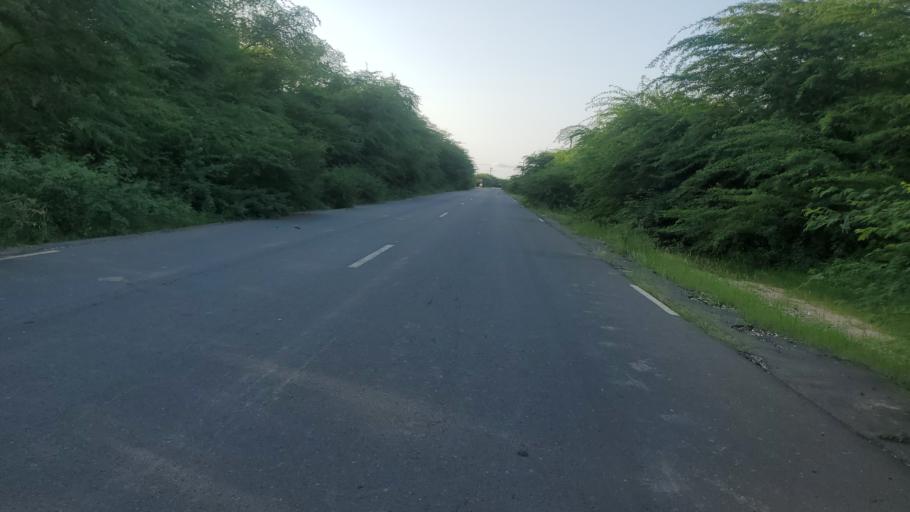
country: SN
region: Saint-Louis
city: Saint-Louis
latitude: 16.2028
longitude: -16.4131
